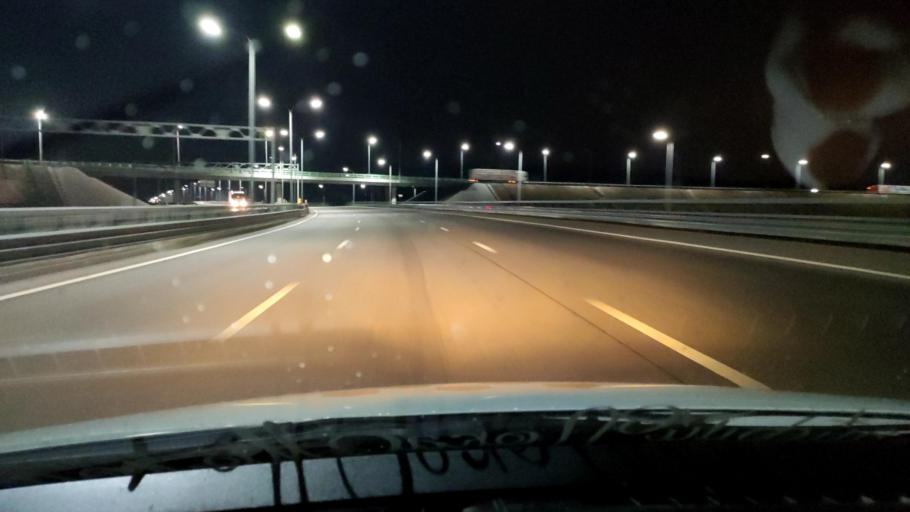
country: RU
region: Voronezj
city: Podgornoye
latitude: 51.8399
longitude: 39.2162
